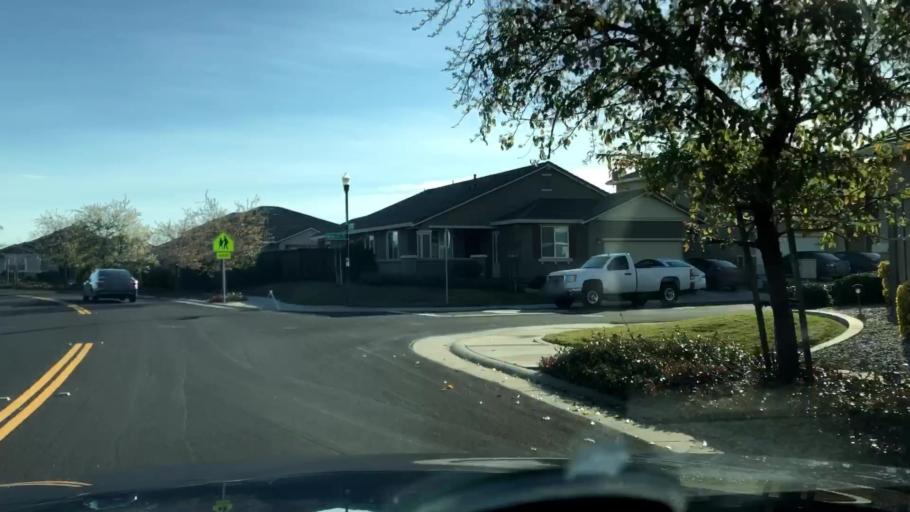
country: US
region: California
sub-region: Sacramento County
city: Laguna
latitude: 38.4011
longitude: -121.4088
